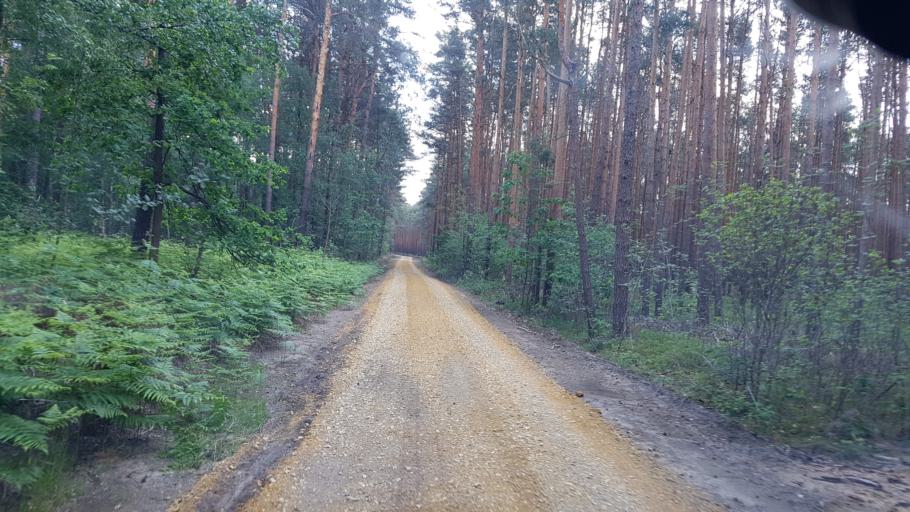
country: DE
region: Brandenburg
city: Ruckersdorf
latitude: 51.5827
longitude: 13.6052
